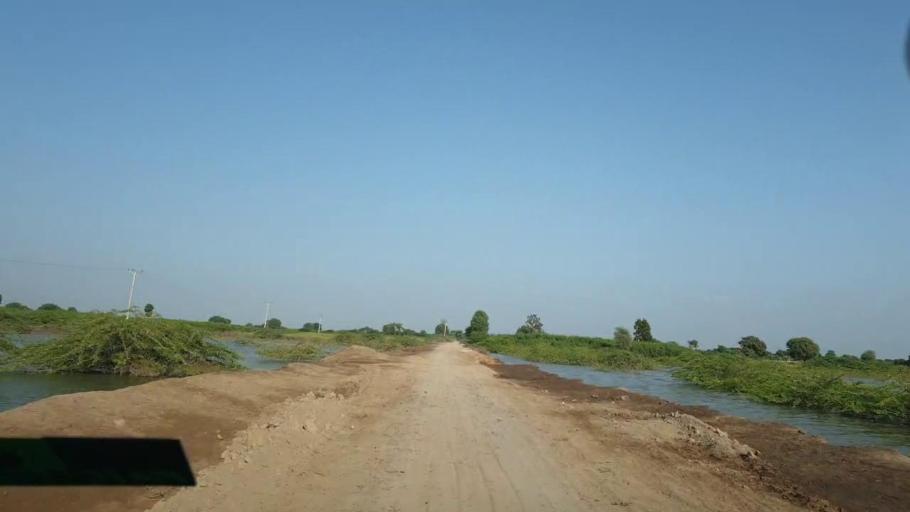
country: PK
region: Sindh
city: Naukot
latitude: 24.7407
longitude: 69.2445
